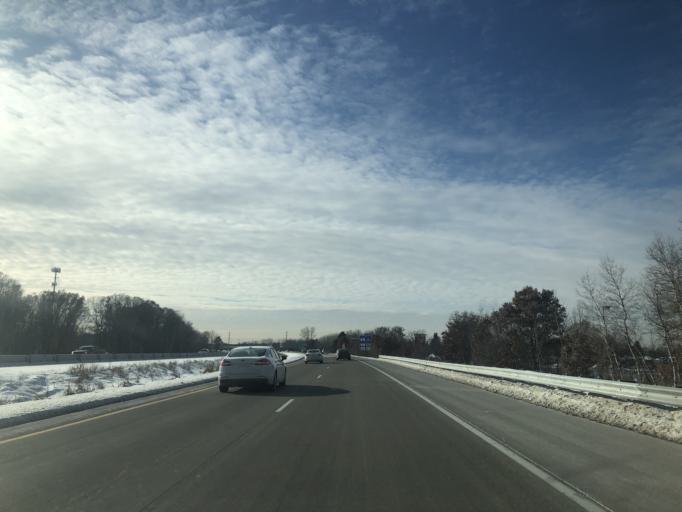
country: US
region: Minnesota
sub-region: Anoka County
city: Circle Pines
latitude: 45.1656
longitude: -93.1534
